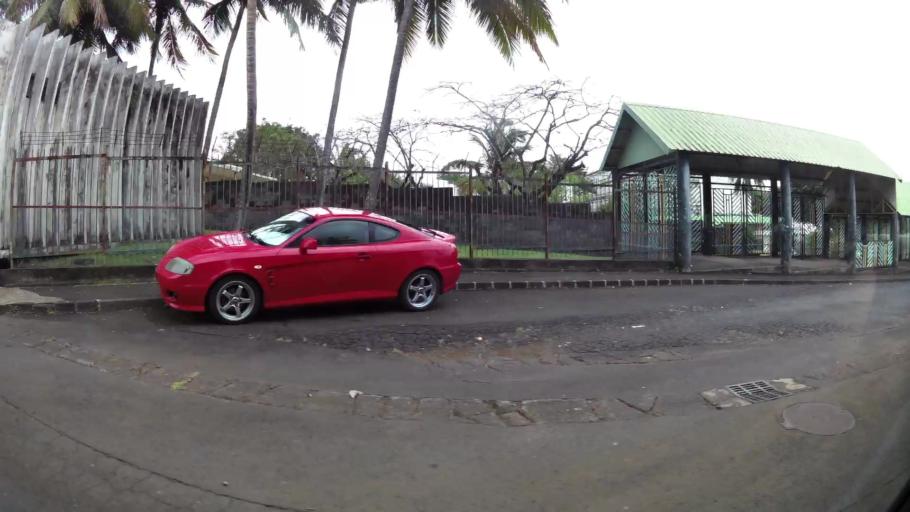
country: RE
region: Reunion
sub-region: Reunion
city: Sainte-Suzanne
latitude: -20.9023
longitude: 55.5992
